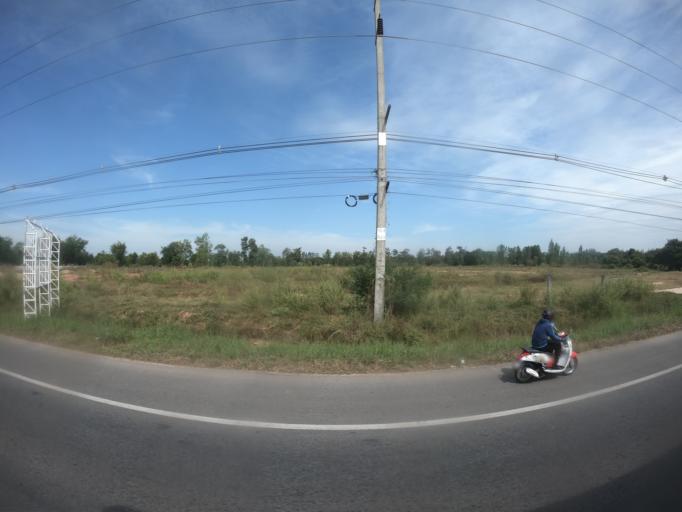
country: TH
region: Maha Sarakham
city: Chiang Yuen
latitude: 16.4450
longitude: 103.0188
